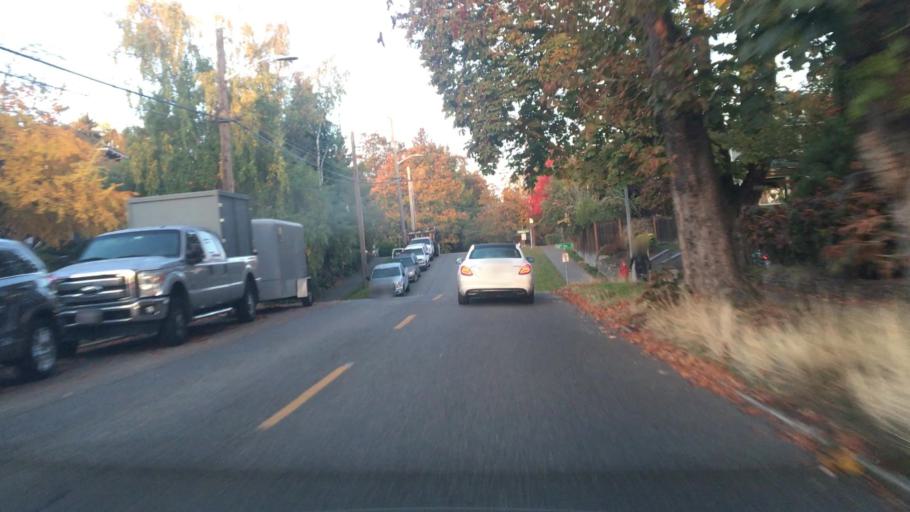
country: US
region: Washington
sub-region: King County
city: Seattle
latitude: 47.6324
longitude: -122.3107
